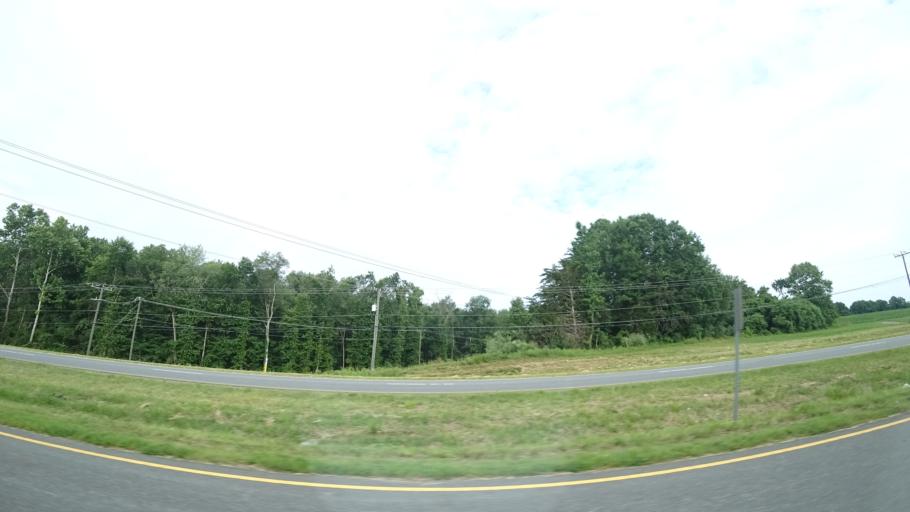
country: US
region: Virginia
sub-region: Spotsylvania County
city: Spotsylvania
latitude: 38.2191
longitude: -77.5690
